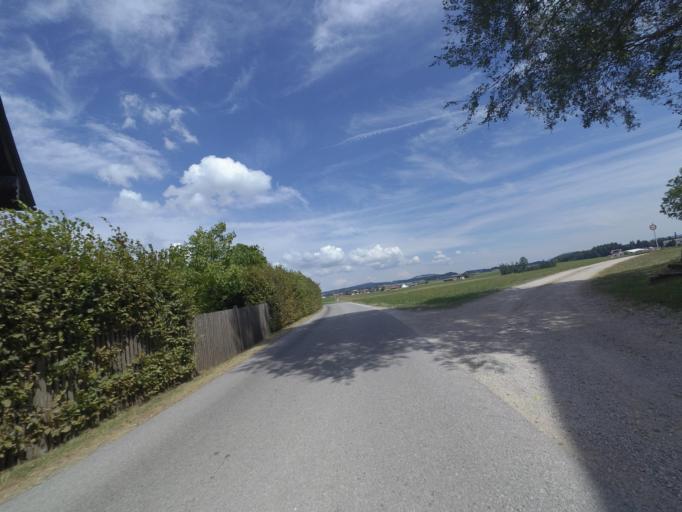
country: AT
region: Salzburg
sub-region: Politischer Bezirk Salzburg-Umgebung
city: Obertrum am See
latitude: 47.9140
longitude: 13.0936
